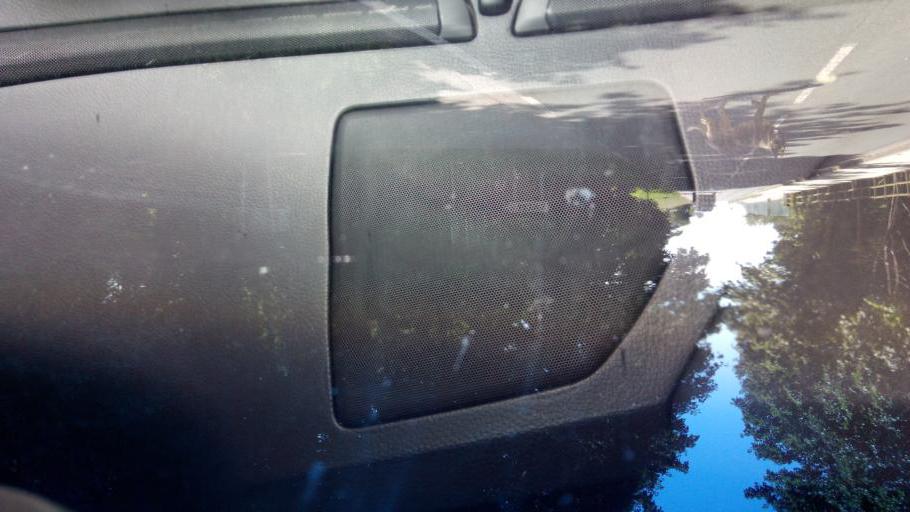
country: ES
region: Asturias
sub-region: Province of Asturias
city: Colunga
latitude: 43.4833
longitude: -5.2512
